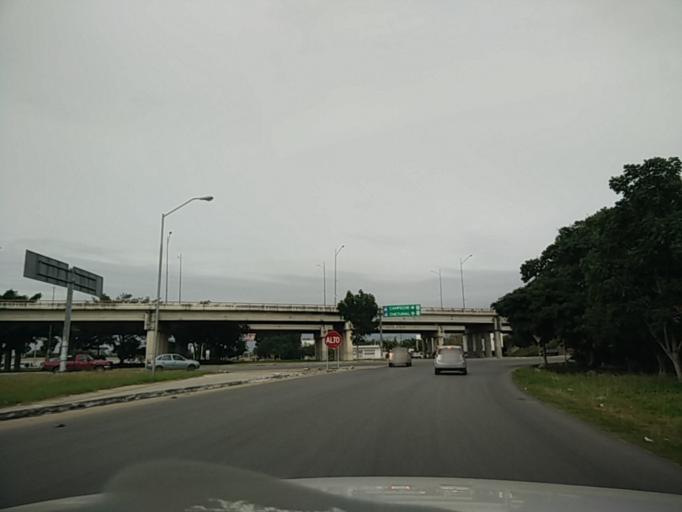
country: MX
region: Yucatan
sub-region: Kanasin
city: Kanasin
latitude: 20.9558
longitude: -89.5685
